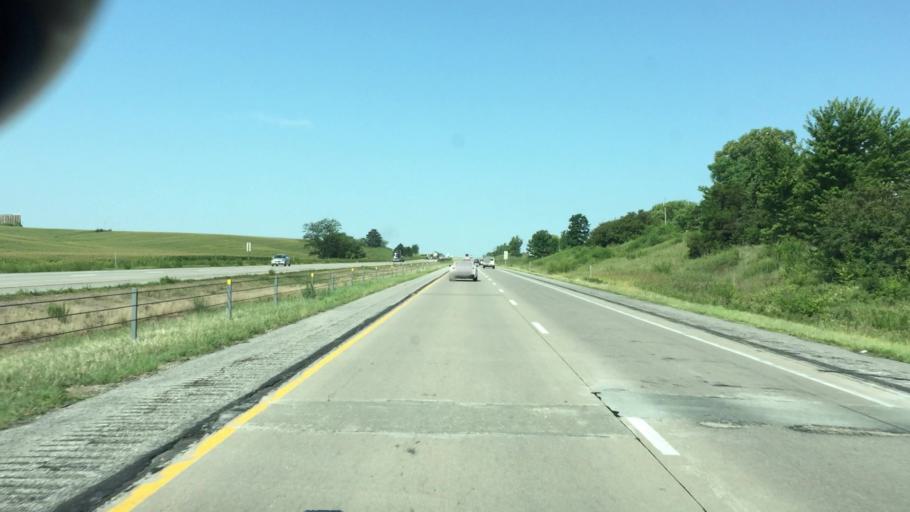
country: US
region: Iowa
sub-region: Iowa County
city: Williamsburg
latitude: 41.6872
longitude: -92.0173
